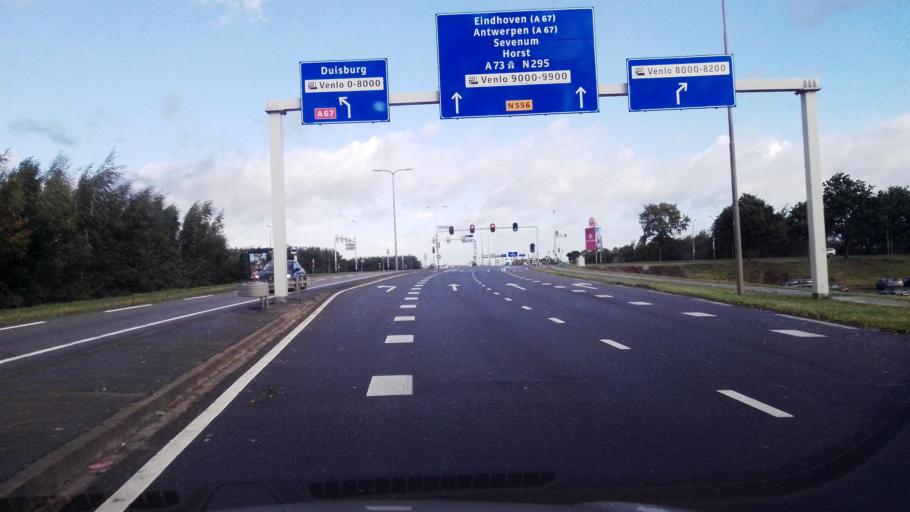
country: NL
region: Limburg
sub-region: Gemeente Peel en Maas
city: Maasbree
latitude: 51.3923
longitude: 6.0843
